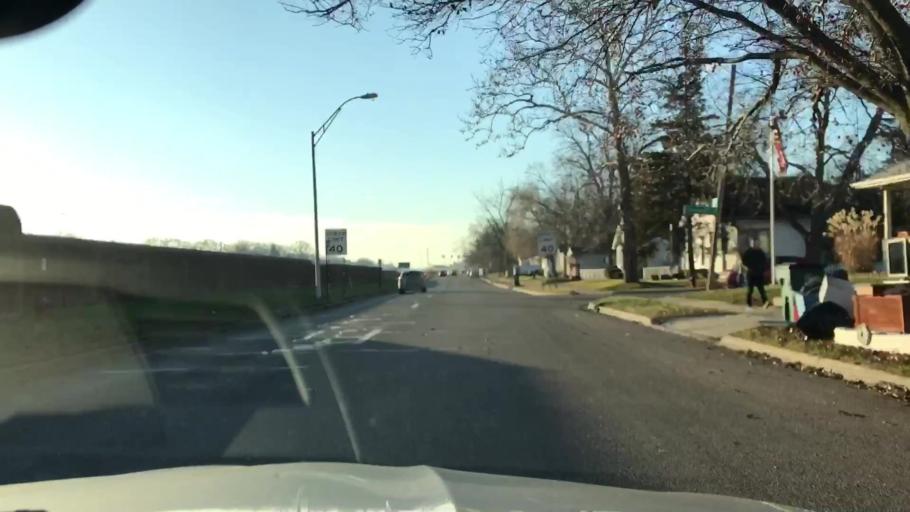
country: US
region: Michigan
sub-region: Oakland County
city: Madison Heights
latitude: 42.4765
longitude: -83.1203
